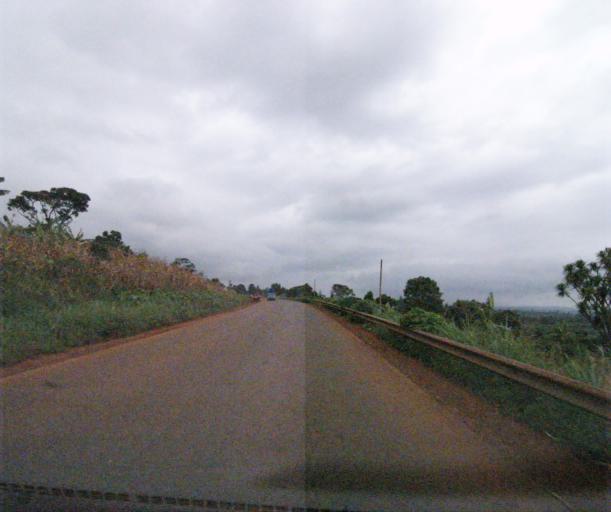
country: CM
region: West
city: Bansoa
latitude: 5.4943
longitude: 10.2257
